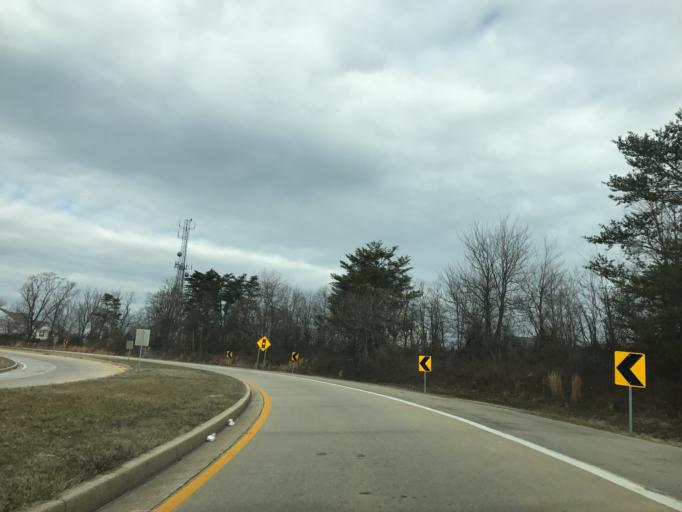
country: US
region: Maryland
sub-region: Anne Arundel County
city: Pumphrey
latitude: 39.2070
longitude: -76.6396
